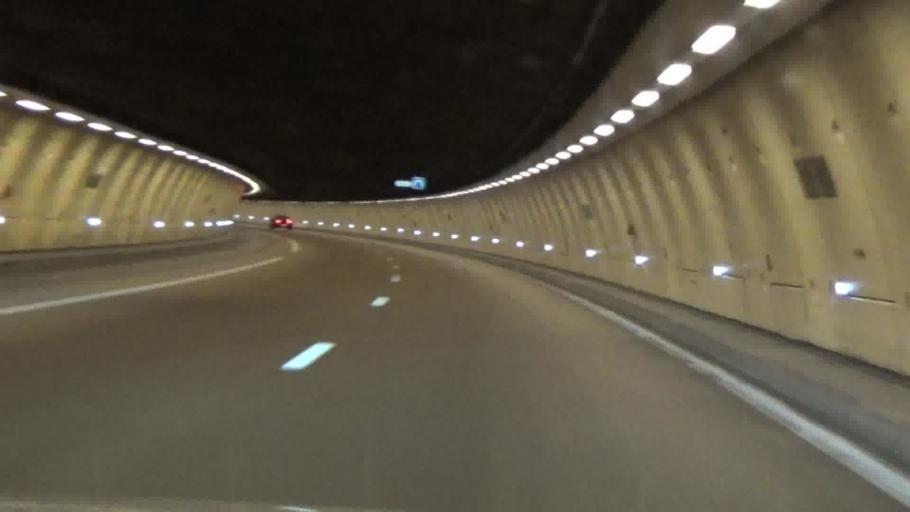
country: FR
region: Ile-de-France
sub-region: Departement des Yvelines
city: Bougival
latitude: 48.8622
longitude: 2.1600
